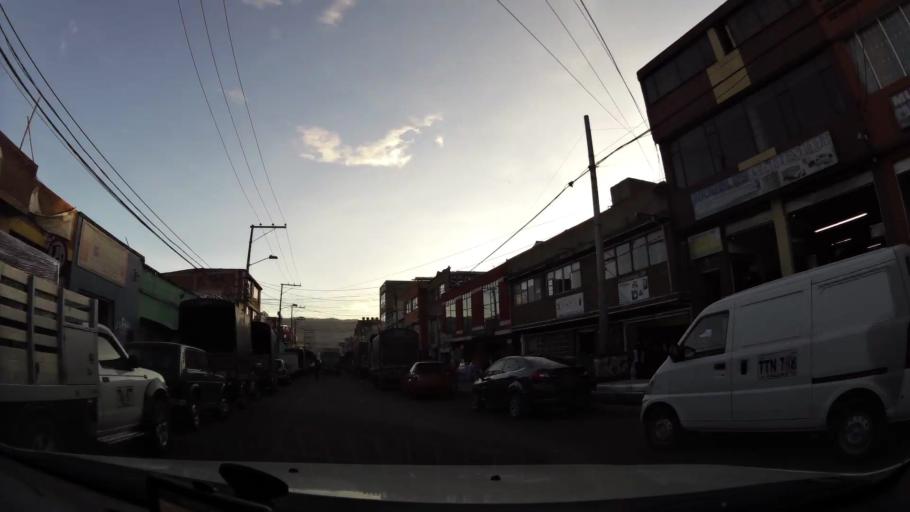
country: CO
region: Bogota D.C.
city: Bogota
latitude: 4.5656
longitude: -74.1274
